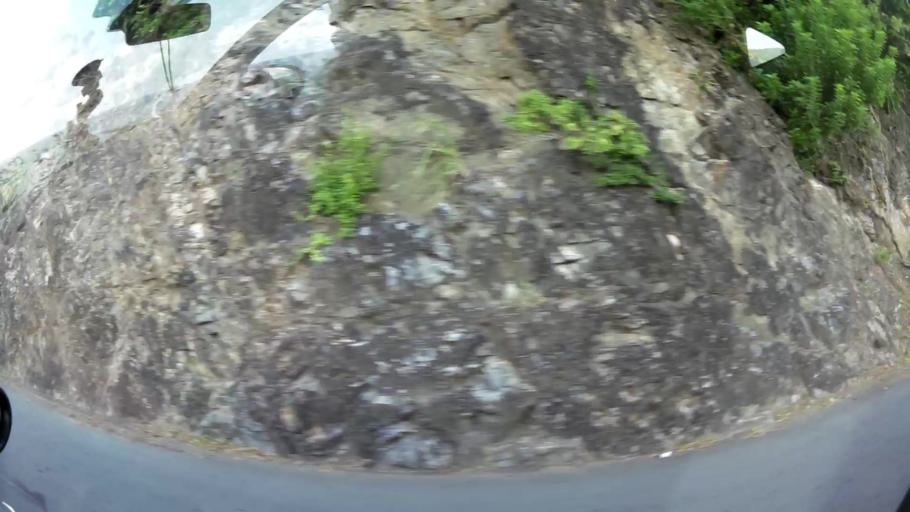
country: TT
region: Eastern Tobago
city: Roxborough
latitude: 11.2341
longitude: -60.5960
